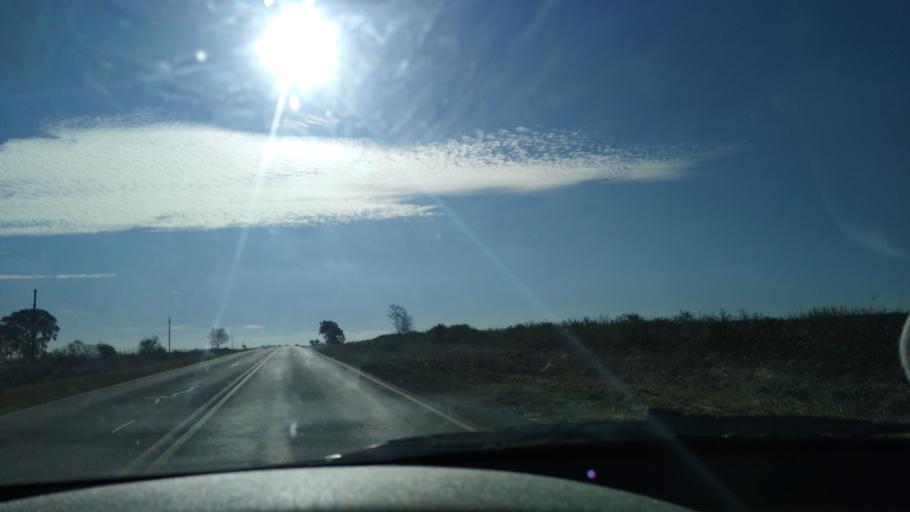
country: AR
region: Entre Rios
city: Aranguren
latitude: -32.3577
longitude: -60.3540
